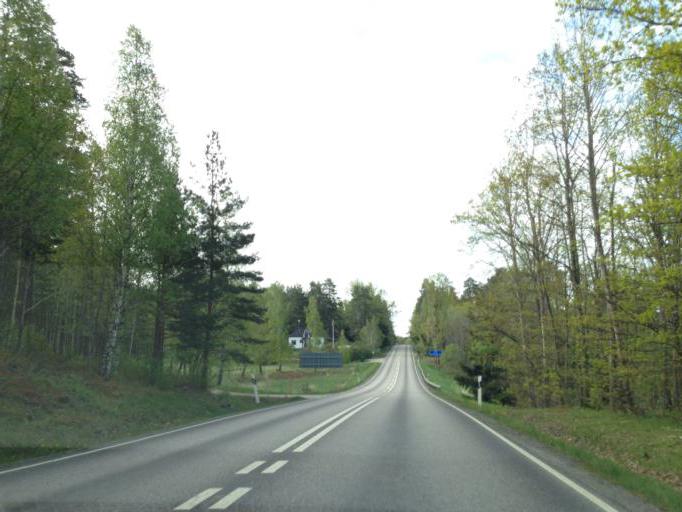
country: SE
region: Soedermanland
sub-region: Flens Kommun
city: Malmkoping
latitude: 59.0657
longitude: 16.8193
